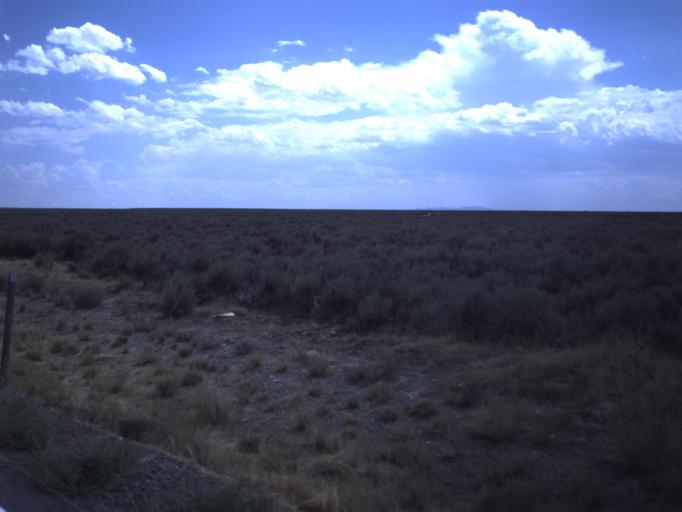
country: US
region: Utah
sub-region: Tooele County
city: Tooele
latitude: 40.3762
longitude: -112.3733
